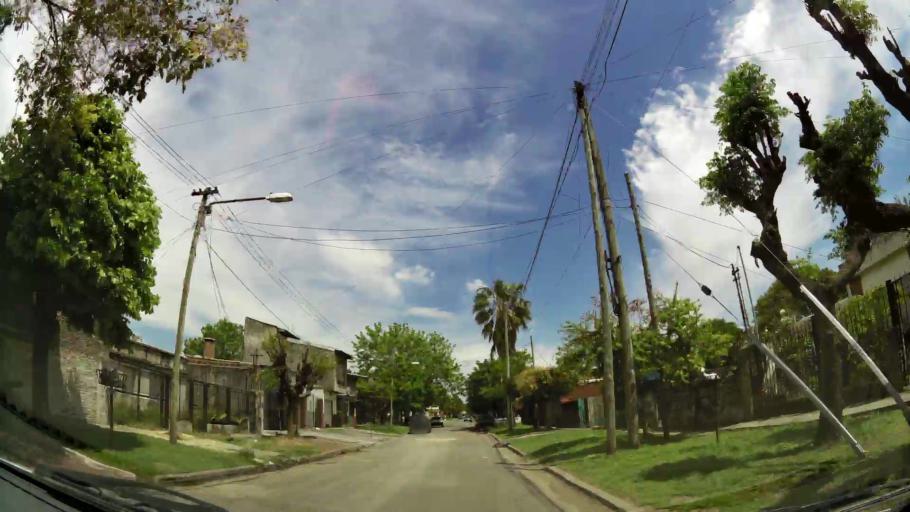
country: AR
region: Buenos Aires
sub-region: Partido de Quilmes
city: Quilmes
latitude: -34.7760
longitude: -58.2564
